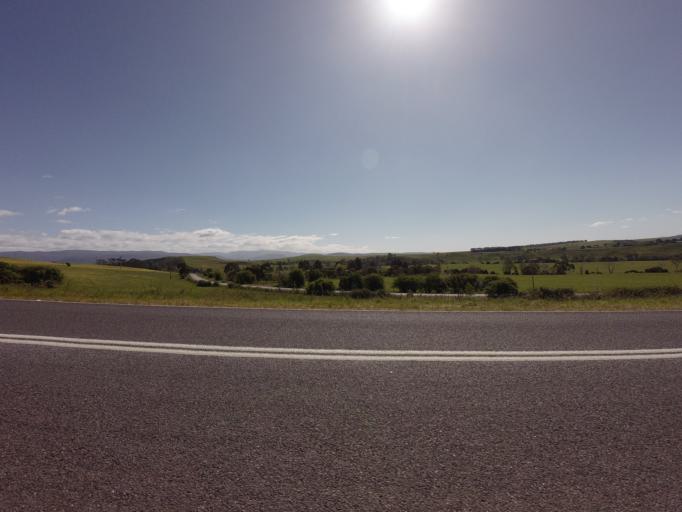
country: AU
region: Tasmania
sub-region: Derwent Valley
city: New Norfolk
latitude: -42.6933
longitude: 146.9400
